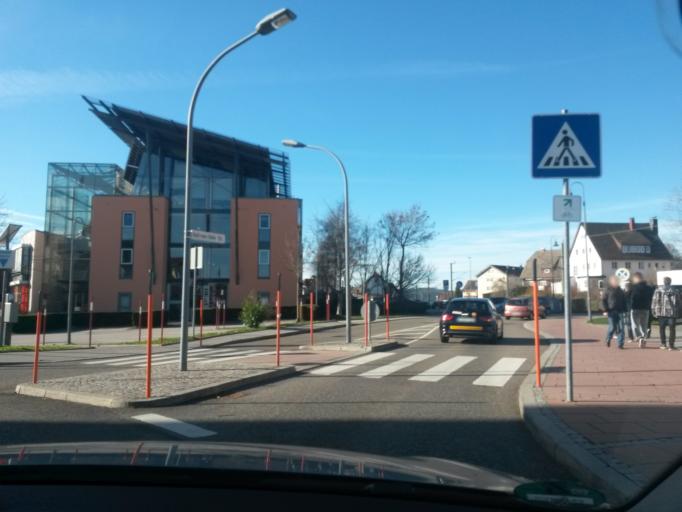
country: DE
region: Baden-Wuerttemberg
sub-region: Karlsruhe Region
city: Freudenstadt
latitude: 48.4672
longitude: 8.4099
